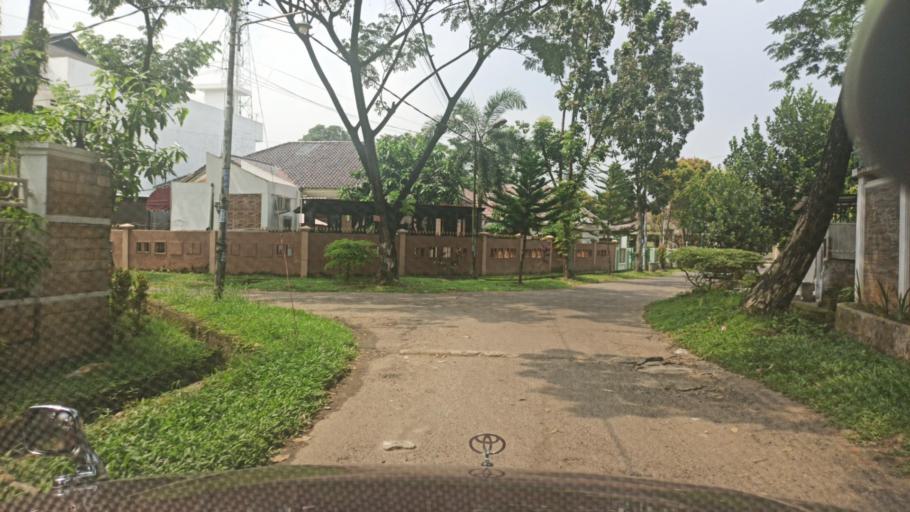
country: ID
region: South Sumatra
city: Plaju
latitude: -2.9892
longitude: 104.7414
